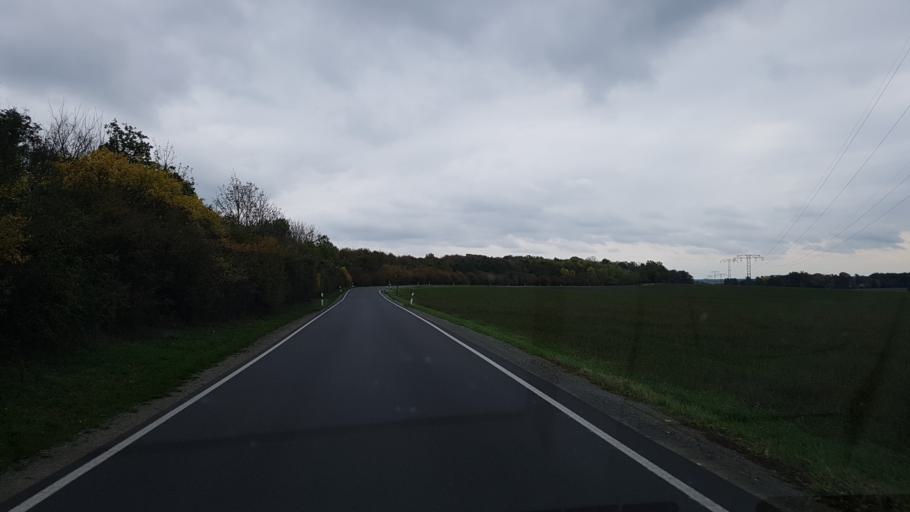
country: DE
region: Saxony
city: Falkenhain
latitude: 51.3870
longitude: 12.8959
